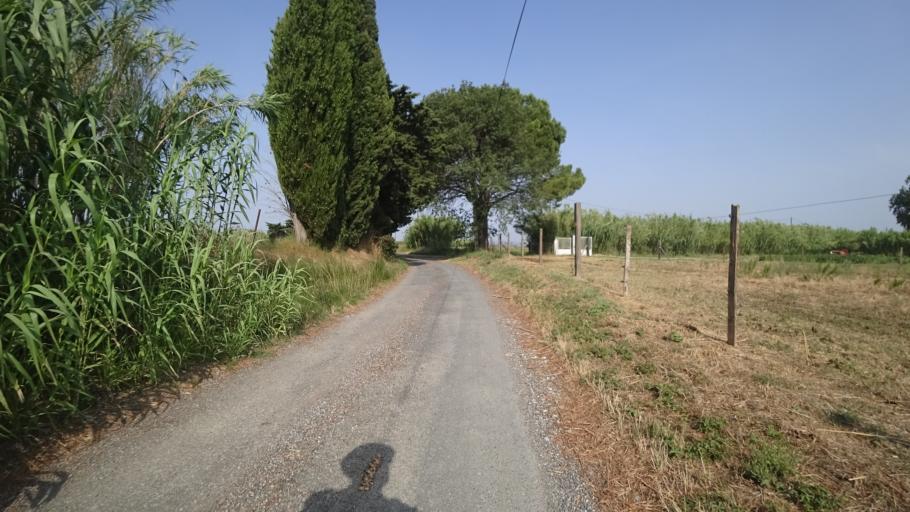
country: FR
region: Languedoc-Roussillon
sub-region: Departement des Pyrenees-Orientales
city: Villelongue-de-la-Salanque
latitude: 42.7350
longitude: 2.9962
